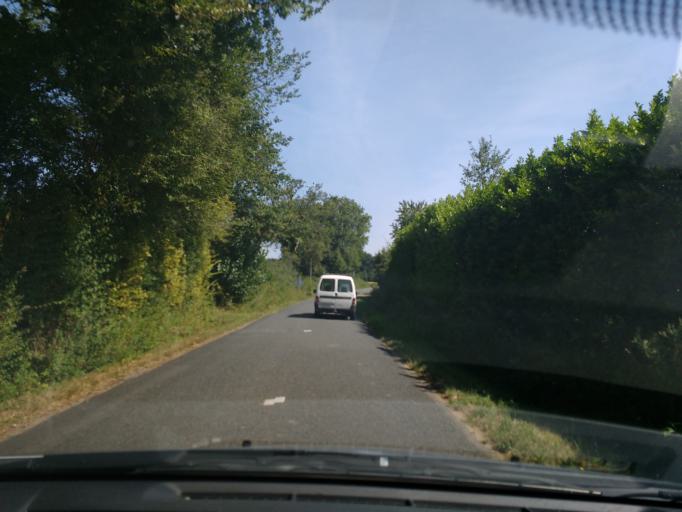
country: FR
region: Pays de la Loire
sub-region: Departement de Maine-et-Loire
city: Beaufort-en-Vallee
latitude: 47.4870
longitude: -0.2179
